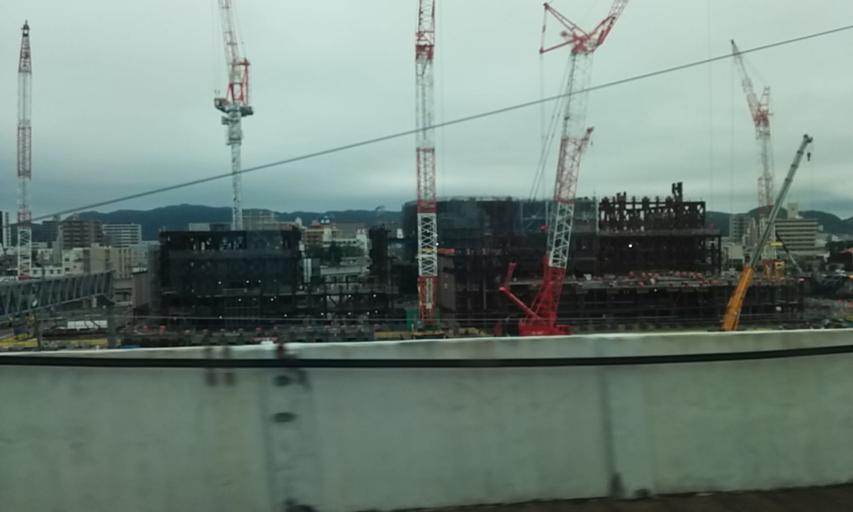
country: JP
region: Hyogo
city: Himeji
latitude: 34.8254
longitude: 134.6995
